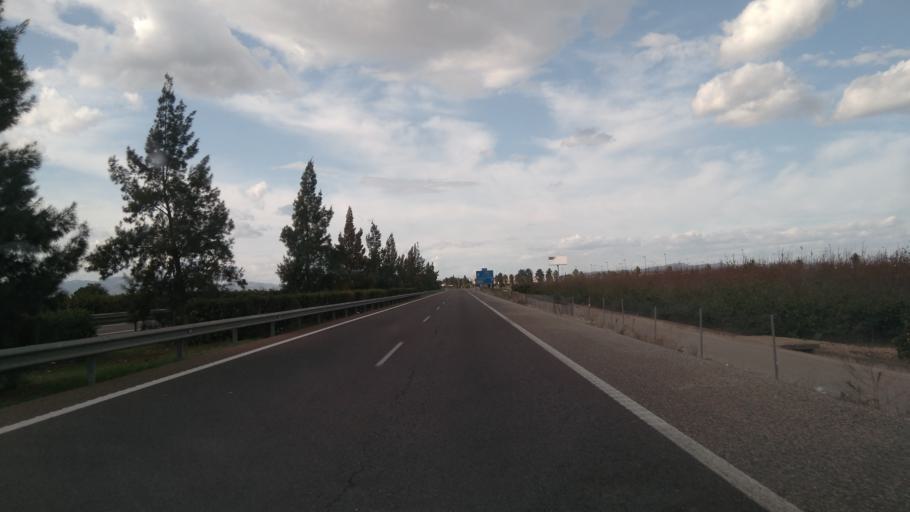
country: ES
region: Valencia
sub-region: Provincia de Valencia
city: Guadassuar
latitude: 39.1712
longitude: -0.4646
